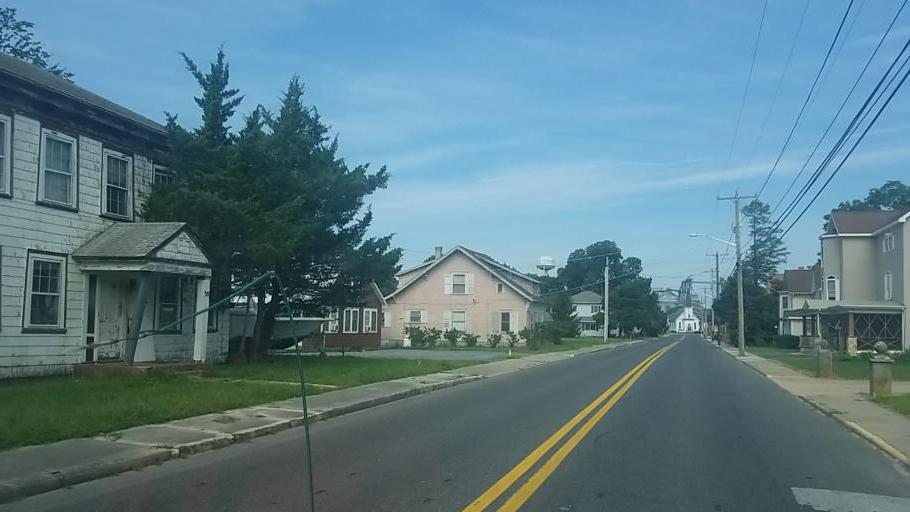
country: US
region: Delaware
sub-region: Sussex County
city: Selbyville
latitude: 38.5165
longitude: -75.2320
